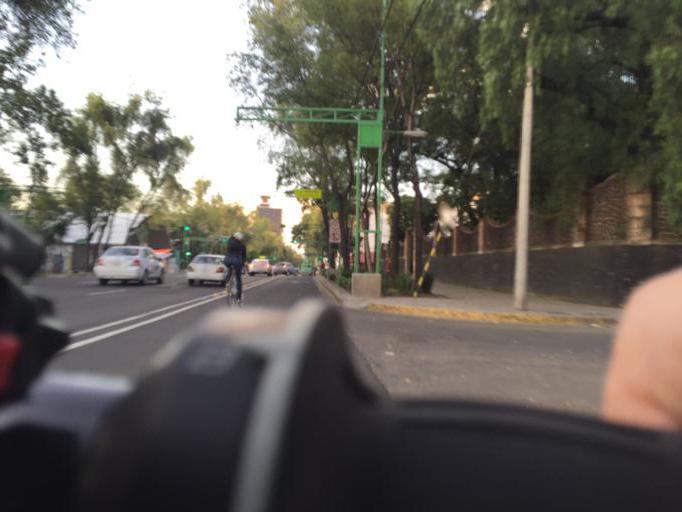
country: MX
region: Mexico City
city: Colonia Nativitas
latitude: 19.3871
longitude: -99.1471
